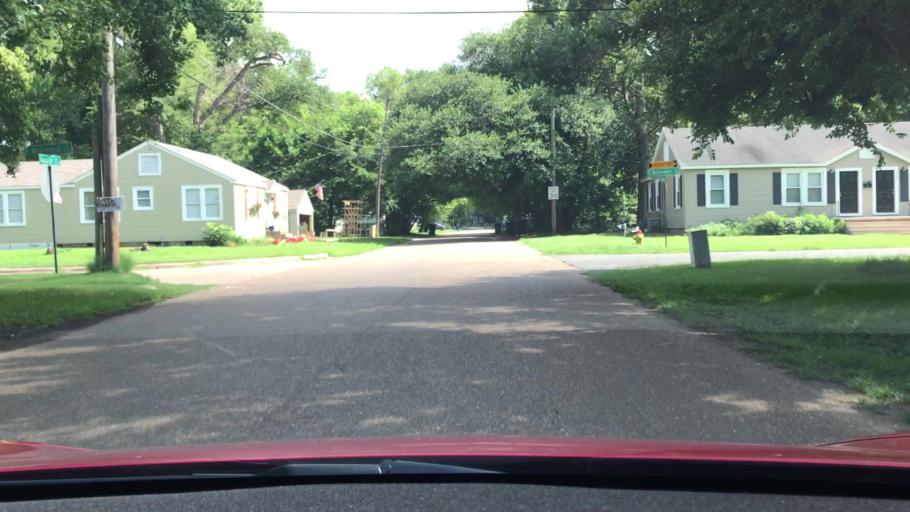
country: US
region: Louisiana
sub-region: Bossier Parish
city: Bossier City
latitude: 32.4738
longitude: -93.7313
